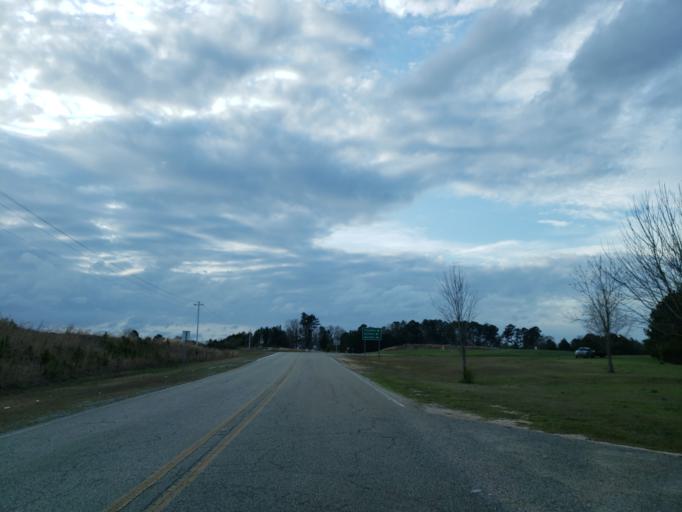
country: US
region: Mississippi
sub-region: Clarke County
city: Stonewall
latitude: 32.2115
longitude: -88.6961
